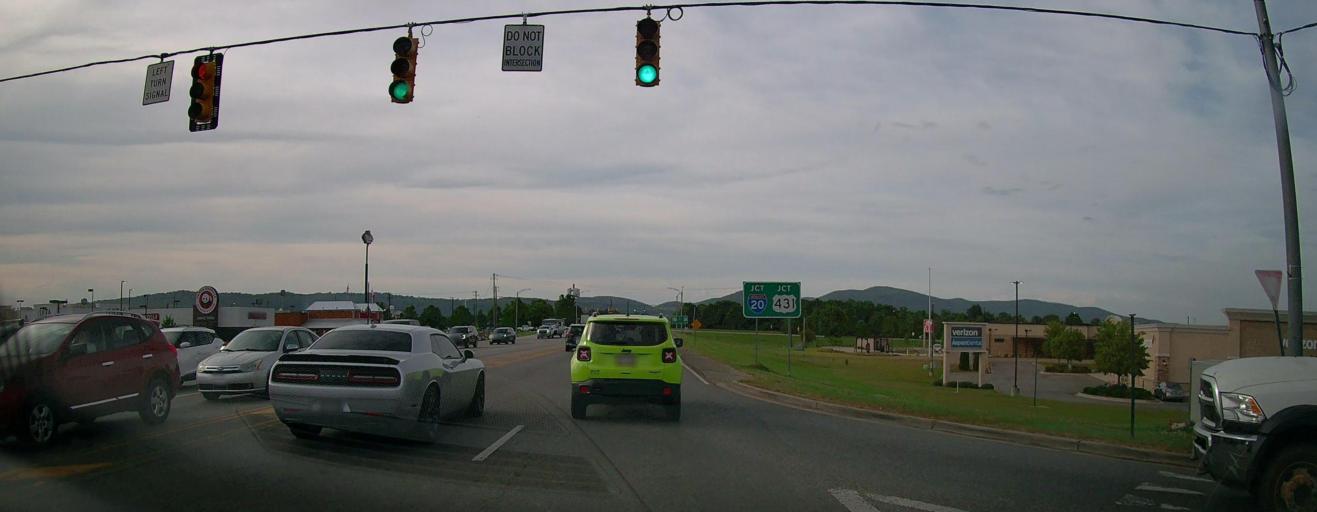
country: US
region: Alabama
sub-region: Calhoun County
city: Oxford
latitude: 33.6079
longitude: -85.7867
